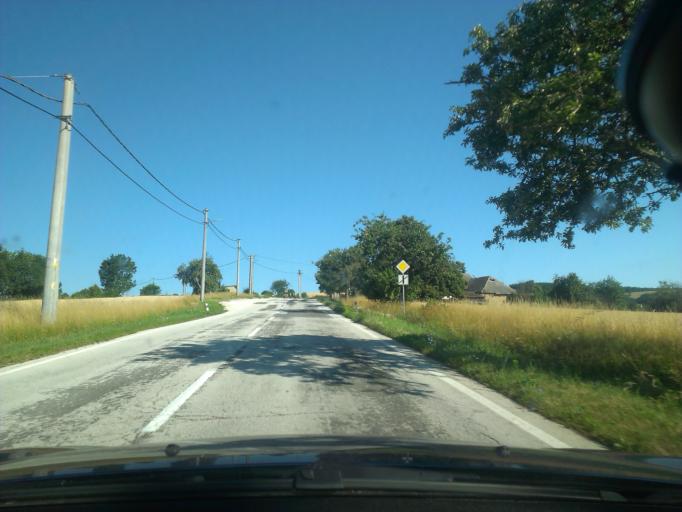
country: SK
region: Trenciansky
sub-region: Okres Myjava
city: Myjava
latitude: 48.7812
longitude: 17.5375
